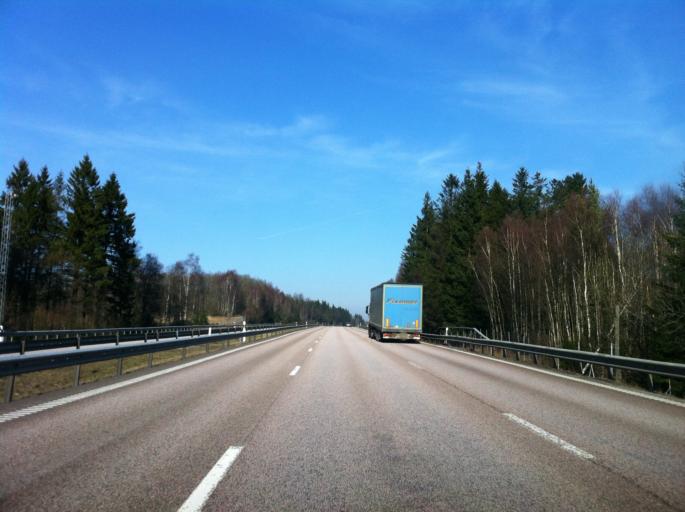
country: SE
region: Skane
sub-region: Bastads Kommun
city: Bastad
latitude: 56.3674
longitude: 12.9345
